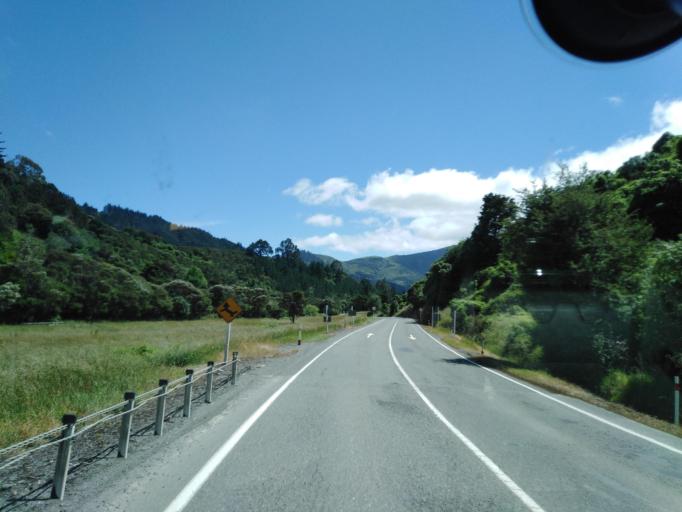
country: NZ
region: Nelson
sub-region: Nelson City
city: Nelson
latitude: -41.2285
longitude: 173.3976
